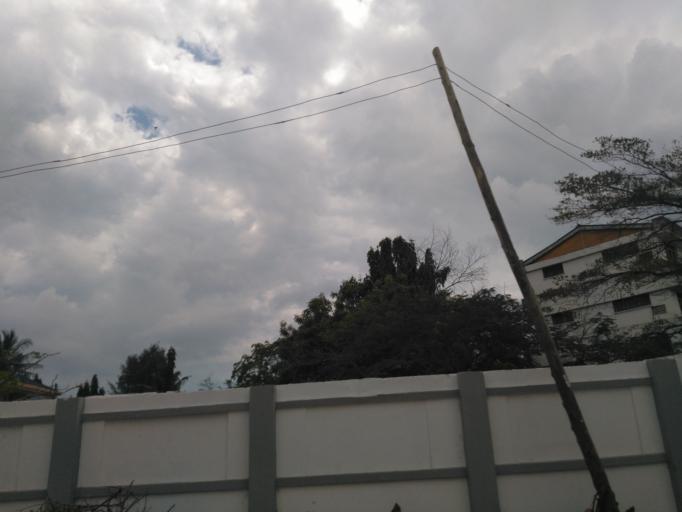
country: TZ
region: Dar es Salaam
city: Magomeni
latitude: -6.7595
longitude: 39.2476
